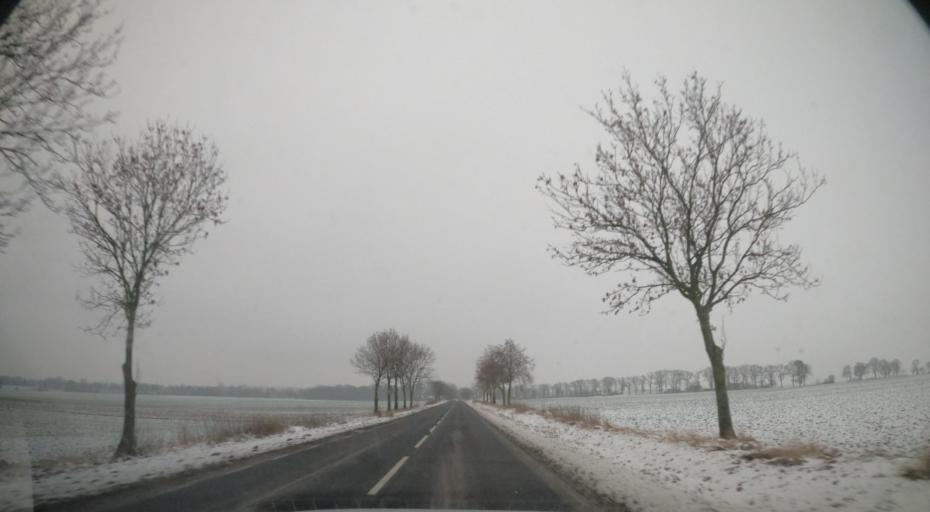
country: PL
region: West Pomeranian Voivodeship
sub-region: Powiat pyrzycki
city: Pyrzyce
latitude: 53.1369
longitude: 14.9524
